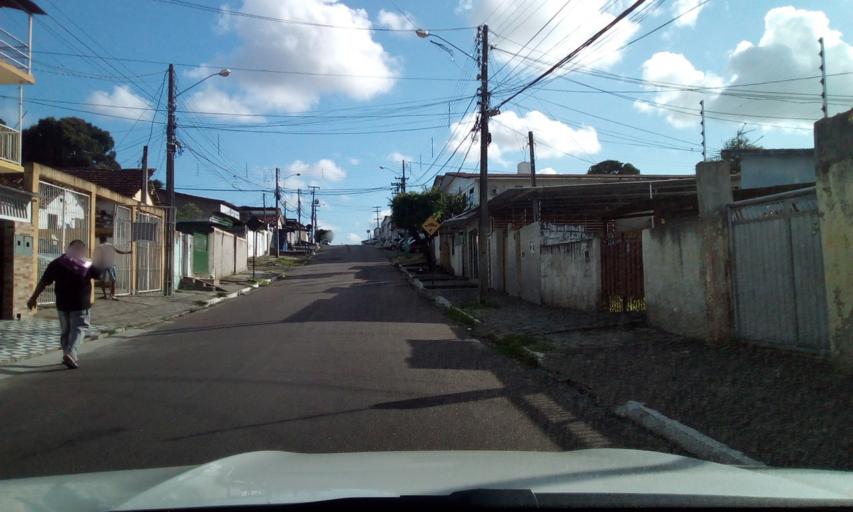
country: BR
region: Paraiba
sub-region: Joao Pessoa
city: Joao Pessoa
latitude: -7.1450
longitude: -34.8909
